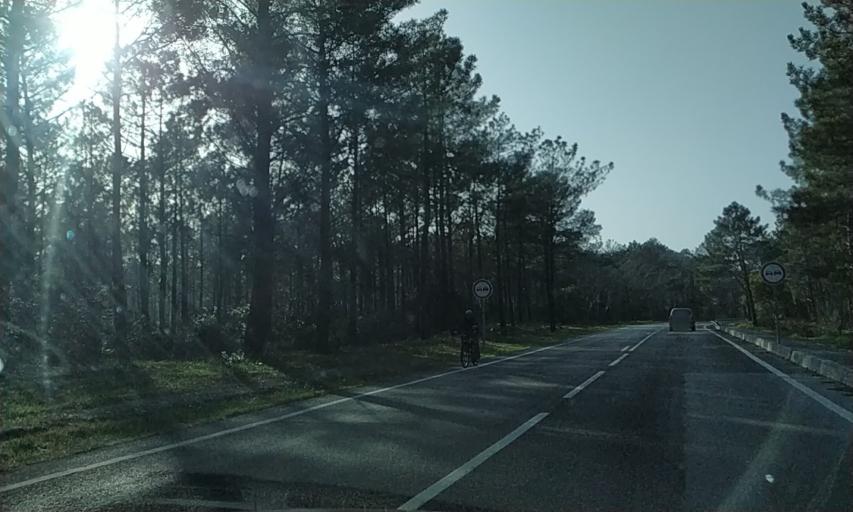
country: PT
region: Leiria
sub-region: Alcobaca
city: Pataias
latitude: 39.7516
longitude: -9.0180
